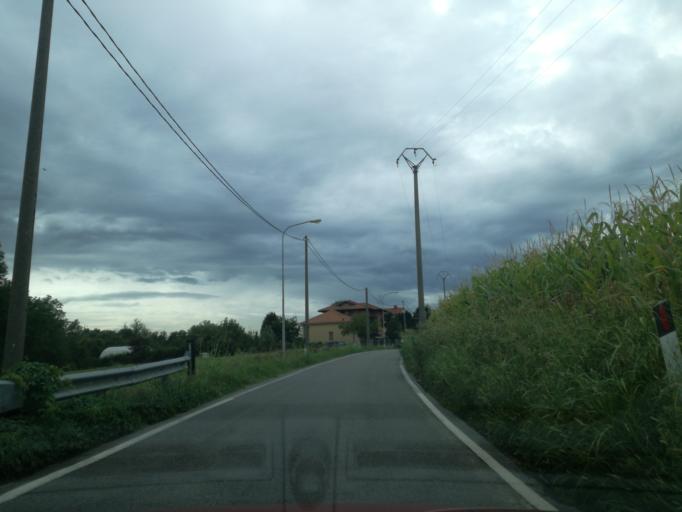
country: IT
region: Lombardy
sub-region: Provincia di Monza e Brianza
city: Cornate d'Adda
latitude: 45.6407
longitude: 9.4615
